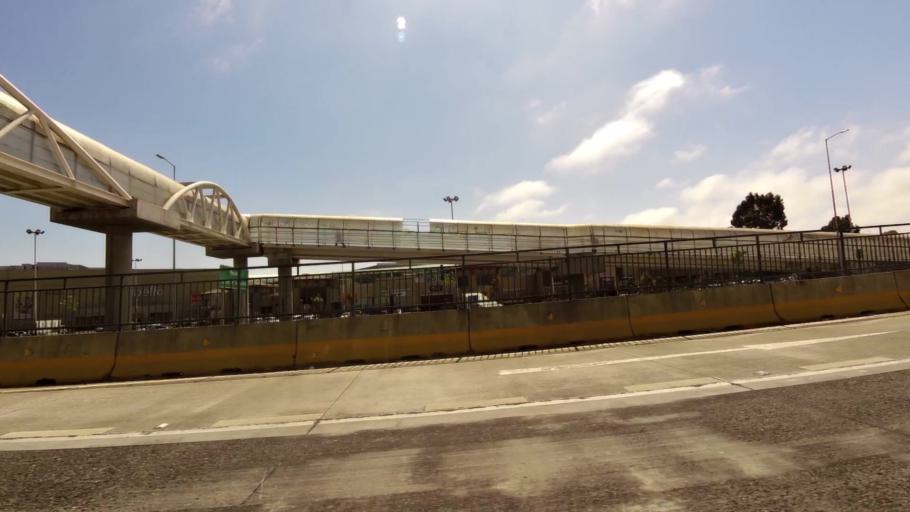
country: CL
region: Biobio
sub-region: Provincia de Concepcion
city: Concepcion
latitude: -36.7929
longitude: -73.0640
